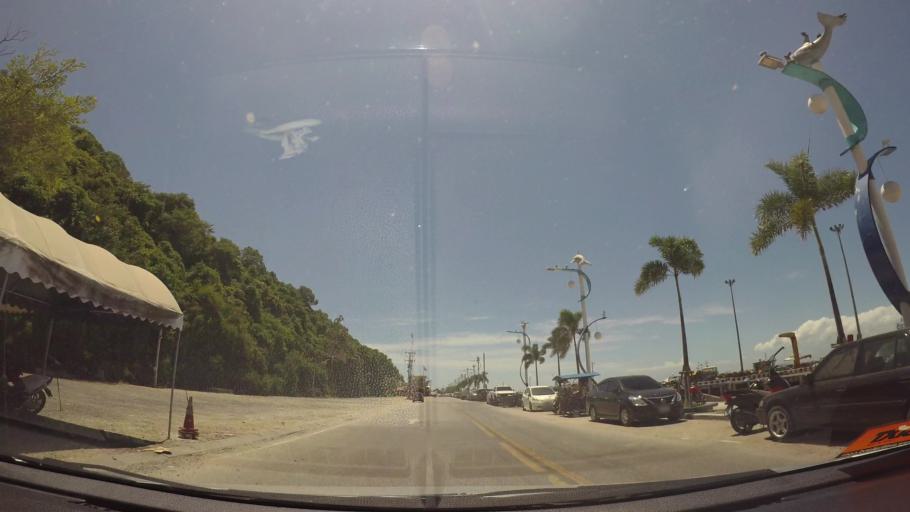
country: TH
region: Chon Buri
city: Phatthaya
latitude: 12.9267
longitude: 100.8645
